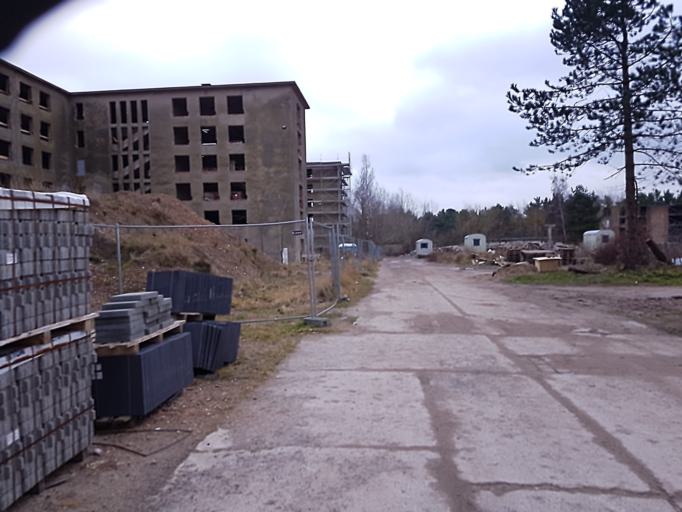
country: DE
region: Mecklenburg-Vorpommern
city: Ostseebad Binz
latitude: 54.4441
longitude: 13.5723
